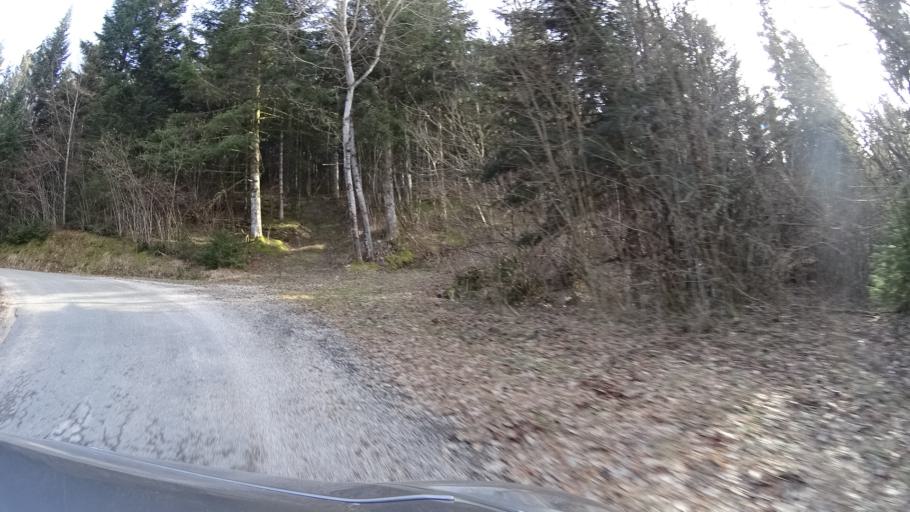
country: FR
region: Franche-Comte
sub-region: Departement du Doubs
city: Pontarlier
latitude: 46.8703
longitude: 6.2662
